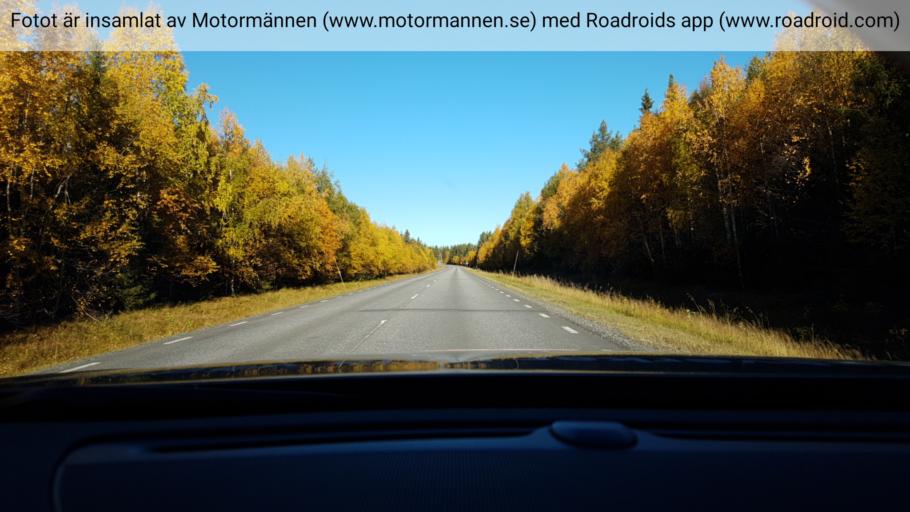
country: SE
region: Vaesterbotten
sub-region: Skelleftea Kommun
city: Storvik
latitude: 65.3799
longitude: 20.3498
